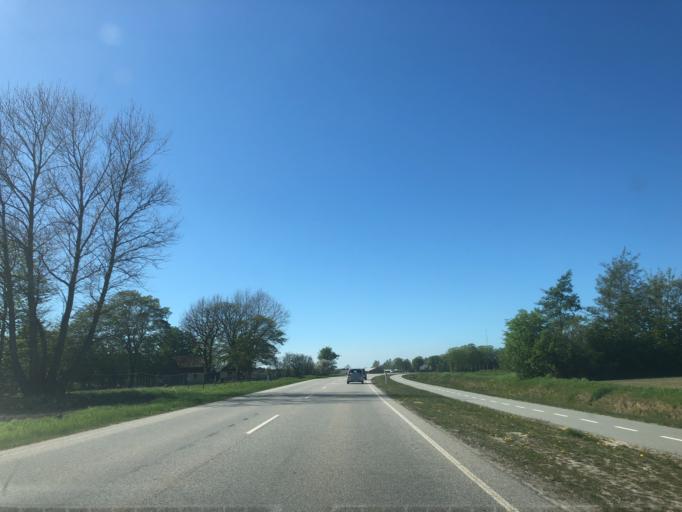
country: DK
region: Zealand
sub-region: Stevns Kommune
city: Store Heddinge
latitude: 55.3544
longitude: 12.3216
